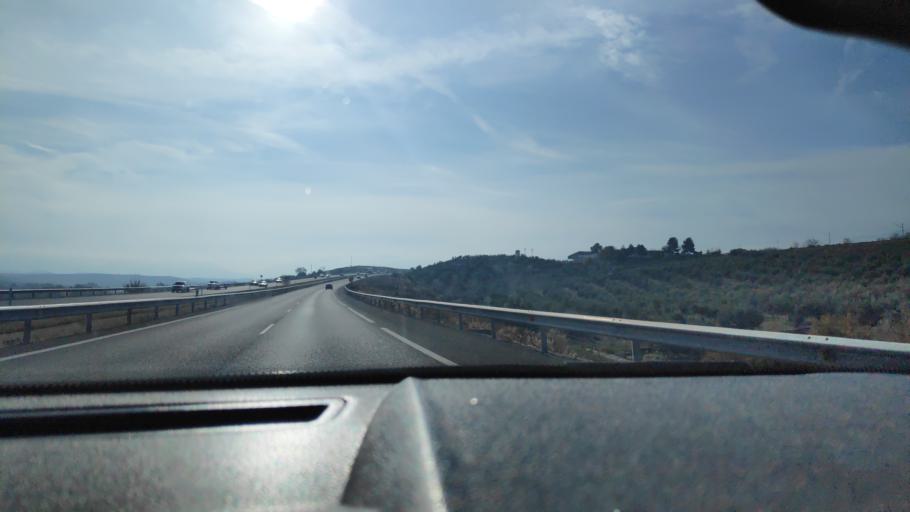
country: ES
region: Andalusia
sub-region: Provincia de Jaen
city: Jaen
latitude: 37.8694
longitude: -3.7655
